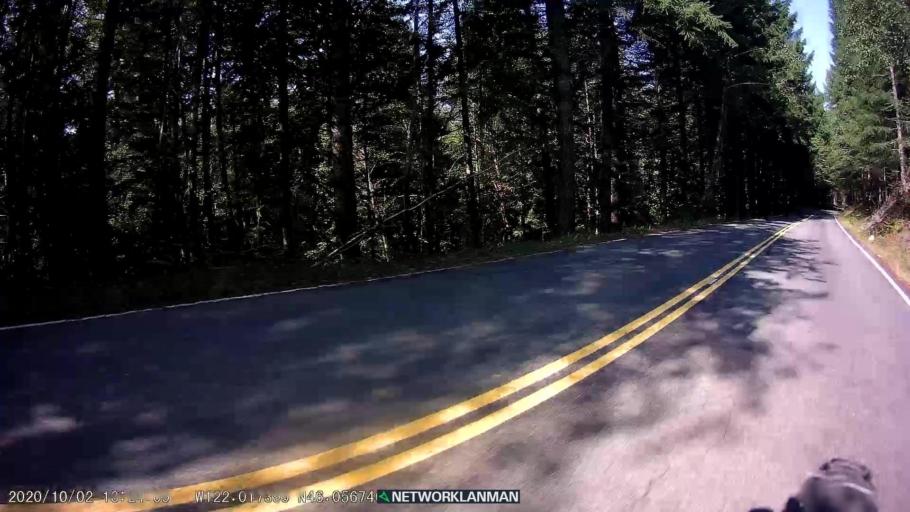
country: US
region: Washington
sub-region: Skamania County
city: Stevenson
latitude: 46.0569
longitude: -122.0175
